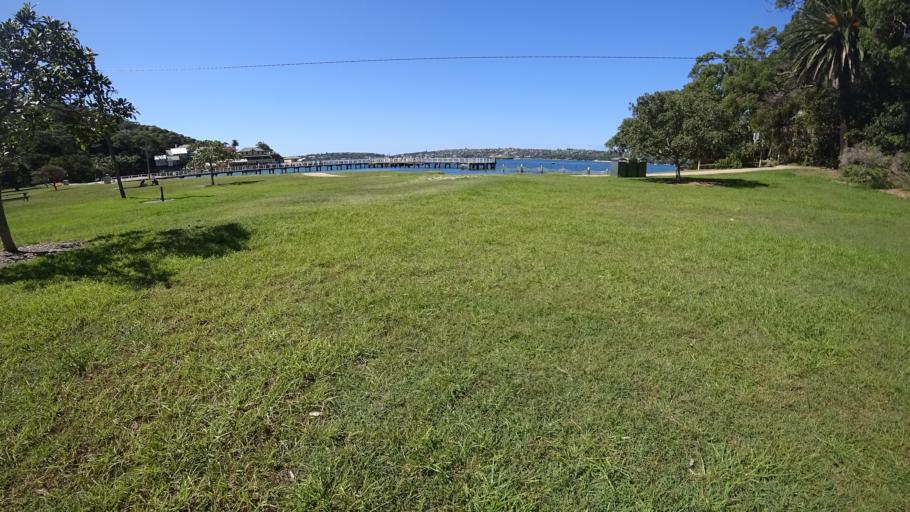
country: AU
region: New South Wales
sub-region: Mosman
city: Mosman
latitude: -33.8397
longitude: 151.2518
